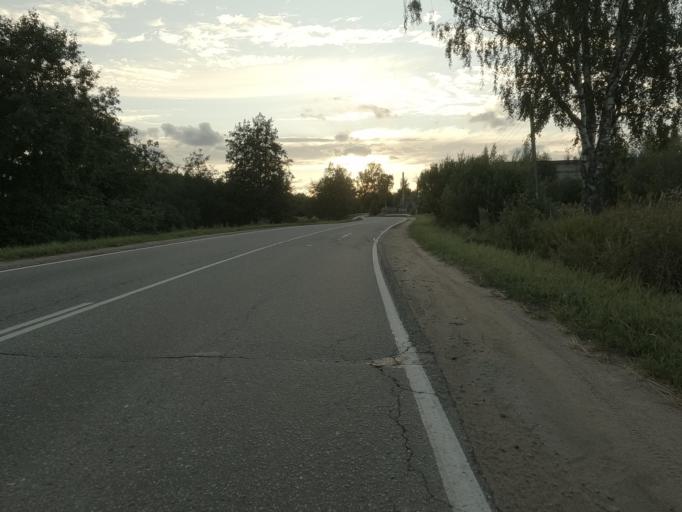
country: RU
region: Leningrad
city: Mga
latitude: 59.7542
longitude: 31.0284
